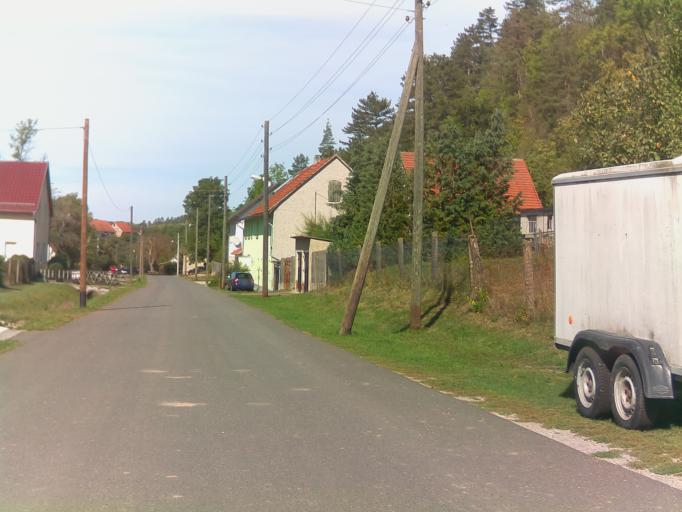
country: DE
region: Thuringia
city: Rottenbach
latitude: 50.7533
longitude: 11.1780
